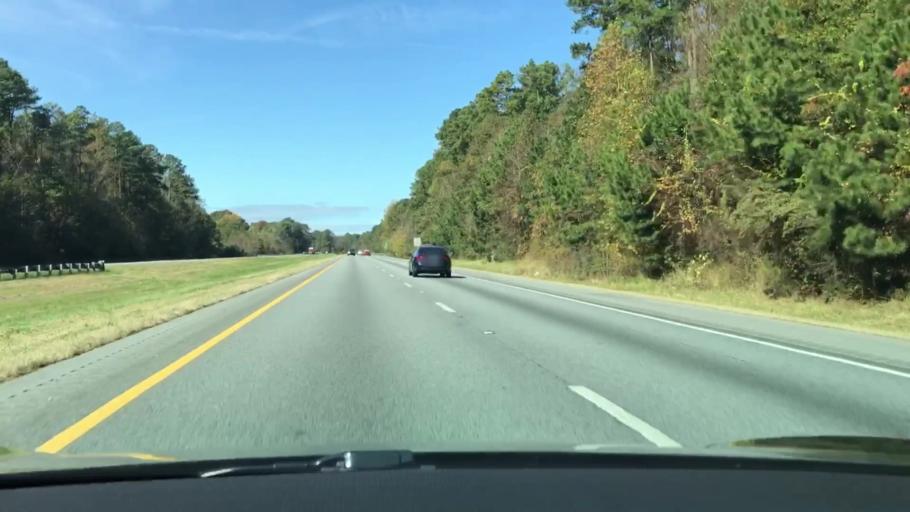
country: US
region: Georgia
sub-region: Morgan County
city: Madison
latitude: 33.5736
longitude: -83.5258
